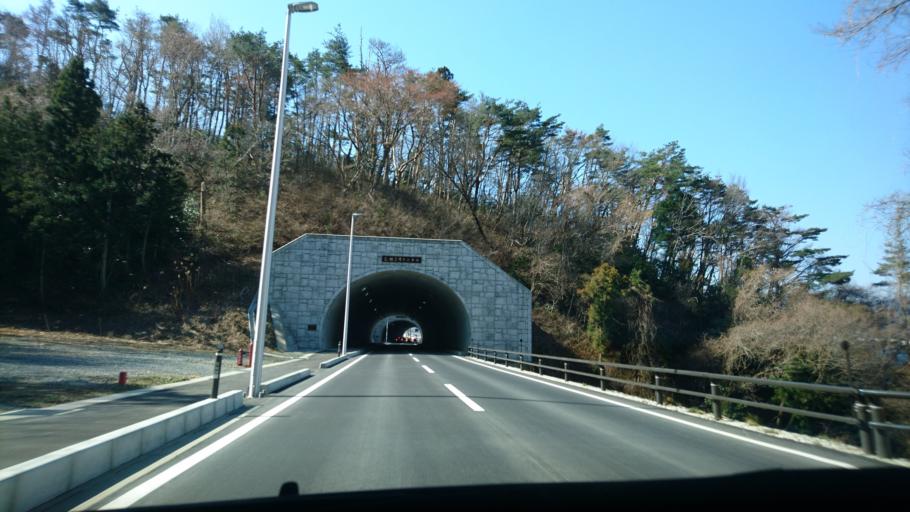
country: JP
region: Iwate
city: Ofunato
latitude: 38.8754
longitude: 141.6050
